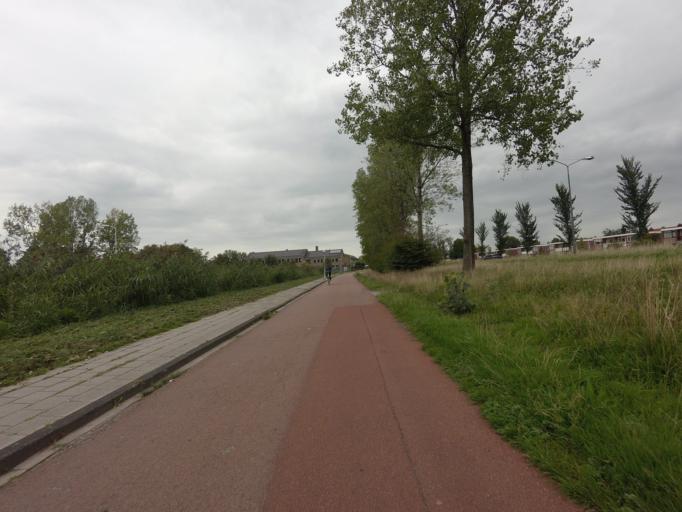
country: NL
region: Friesland
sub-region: Sudwest Fryslan
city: Sneek
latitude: 53.0249
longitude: 5.6552
